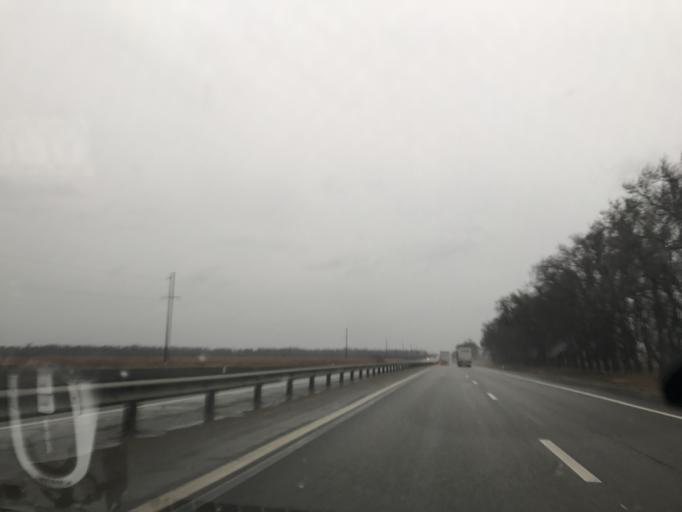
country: RU
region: Krasnodarskiy
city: Kislyakovskaya
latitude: 46.3863
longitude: 39.7413
